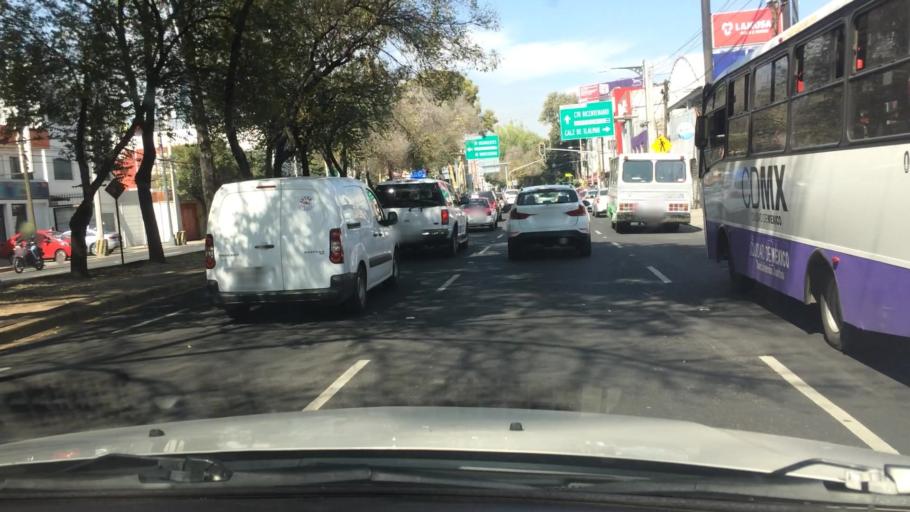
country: MX
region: Mexico City
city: Coyoacan
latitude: 19.3416
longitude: -99.1485
